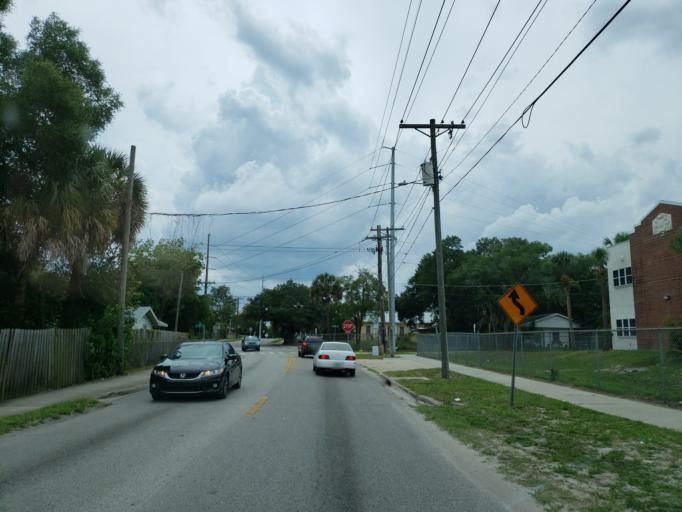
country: US
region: Florida
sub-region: Hillsborough County
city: University
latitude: 28.0253
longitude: -82.4467
